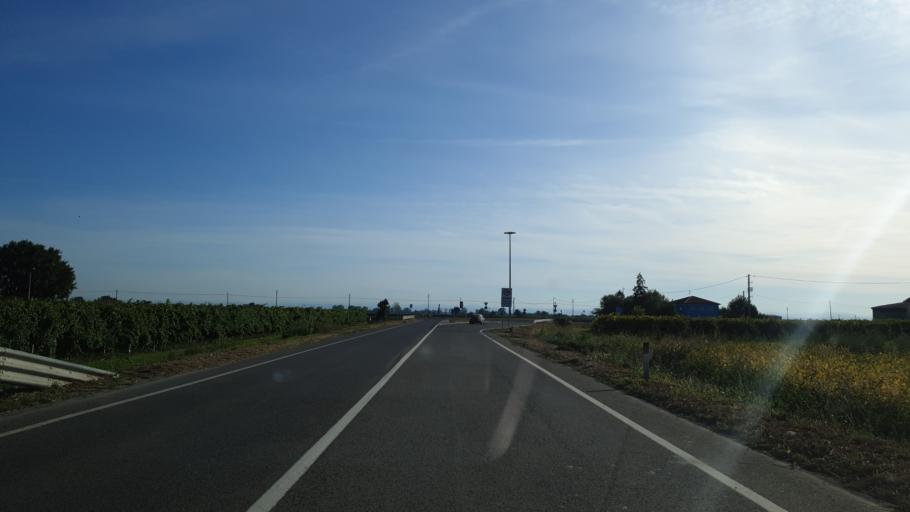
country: IT
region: Emilia-Romagna
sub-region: Provincia di Ferrara
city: Longastrino
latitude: 44.5419
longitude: 11.9970
